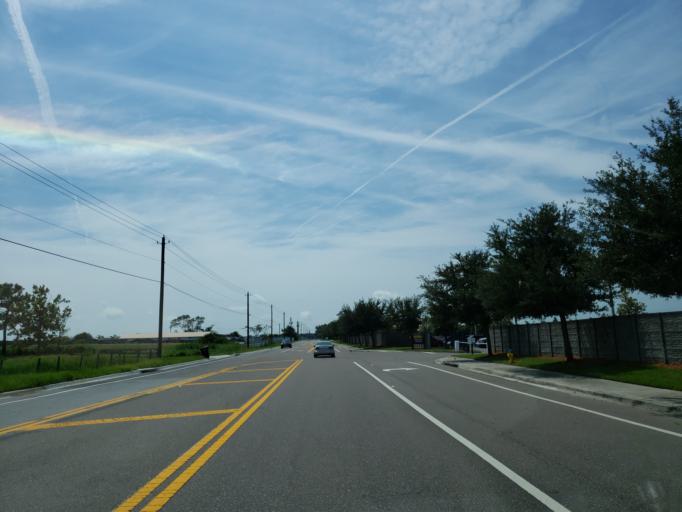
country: US
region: Florida
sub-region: Hillsborough County
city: Riverview
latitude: 27.8453
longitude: -82.3433
